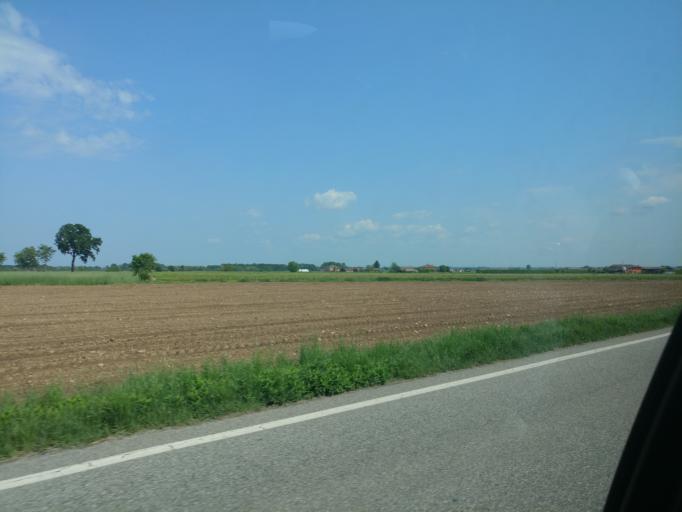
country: IT
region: Piedmont
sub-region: Provincia di Torino
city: Cavour
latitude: 44.7662
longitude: 7.3948
